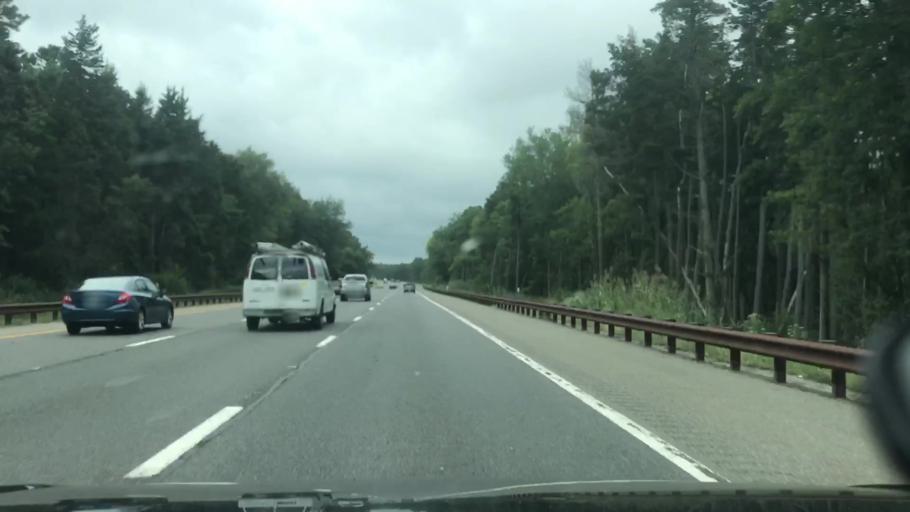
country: US
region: New Jersey
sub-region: Ocean County
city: Forked River
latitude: 39.8358
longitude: -74.2242
